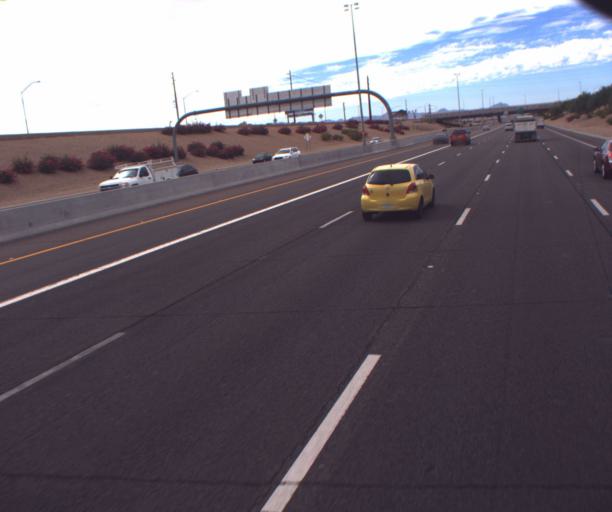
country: US
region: Arizona
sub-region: Maricopa County
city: Chandler
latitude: 33.2920
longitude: -111.9064
